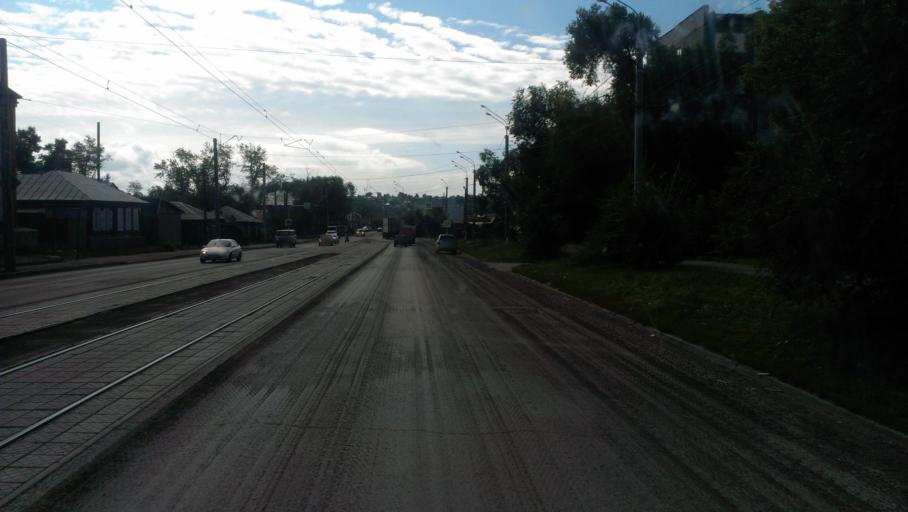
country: RU
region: Altai Krai
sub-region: Gorod Barnaulskiy
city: Barnaul
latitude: 53.3281
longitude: 83.7622
